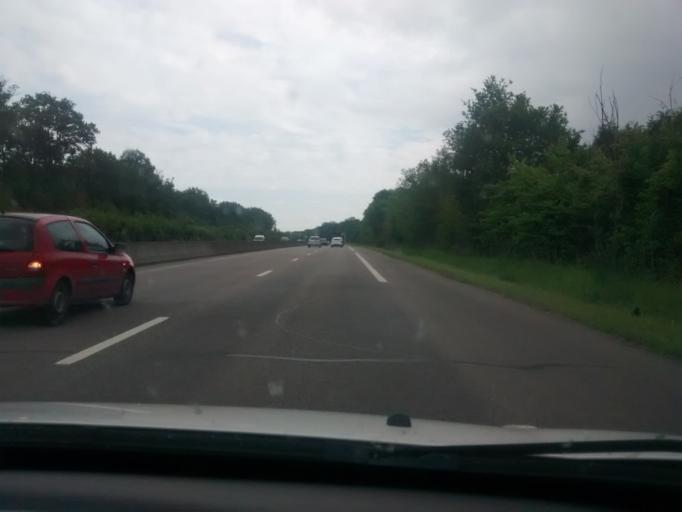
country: FR
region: Ile-de-France
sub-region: Departement des Yvelines
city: Ablis
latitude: 48.5403
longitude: 1.8295
